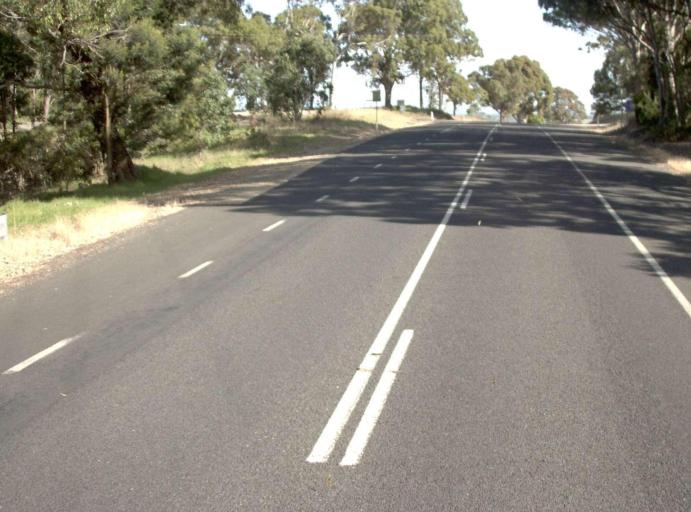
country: AU
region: Victoria
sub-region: East Gippsland
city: Lakes Entrance
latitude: -37.8587
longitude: 147.8455
